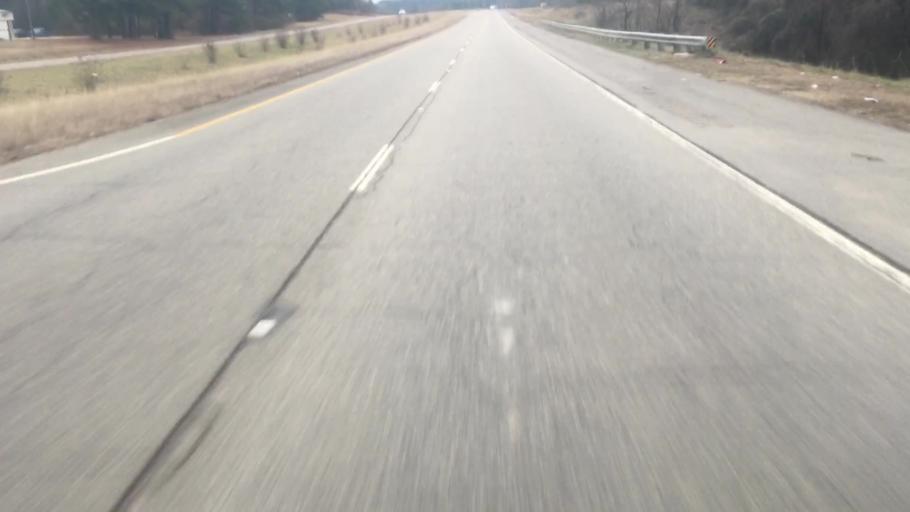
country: US
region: Alabama
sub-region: Walker County
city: Dora
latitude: 33.7994
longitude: -87.1145
